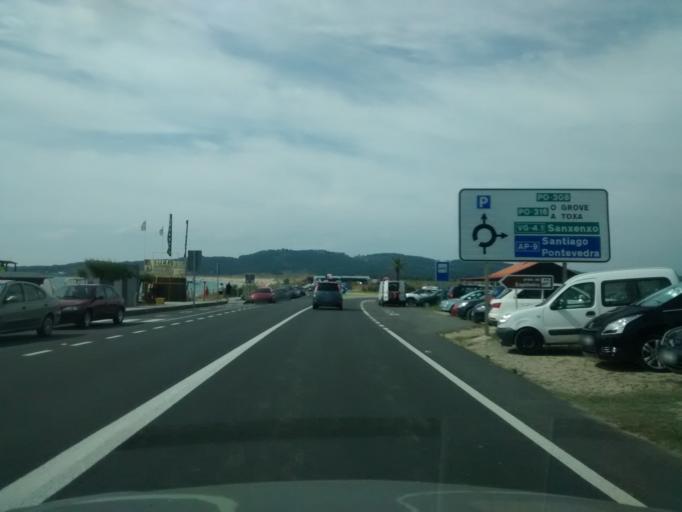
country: ES
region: Galicia
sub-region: Provincia de Pontevedra
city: O Grove
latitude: 42.4383
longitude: -8.8709
